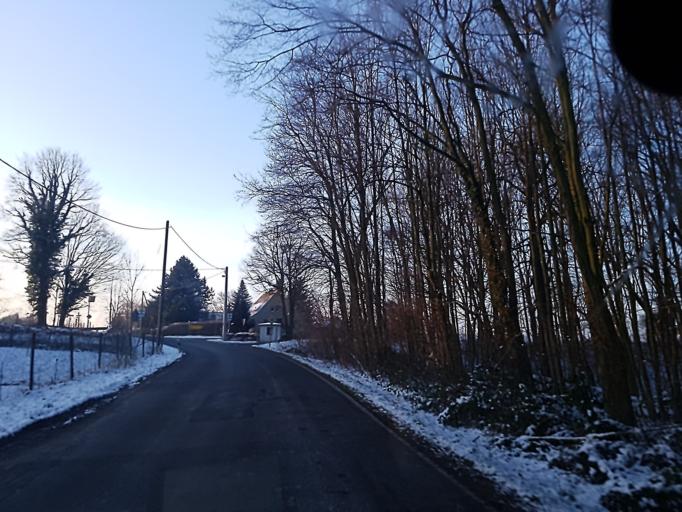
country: DE
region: Saxony
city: Mugeln
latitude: 51.2177
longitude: 13.0328
